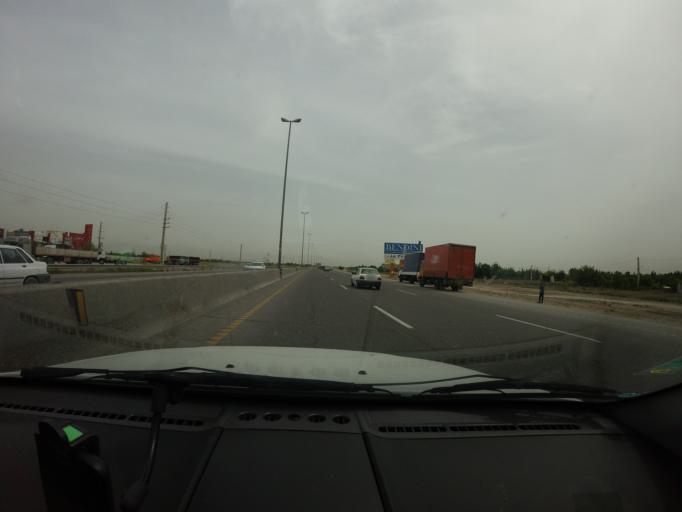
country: IR
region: Tehran
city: Robat Karim
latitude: 35.5214
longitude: 51.0806
